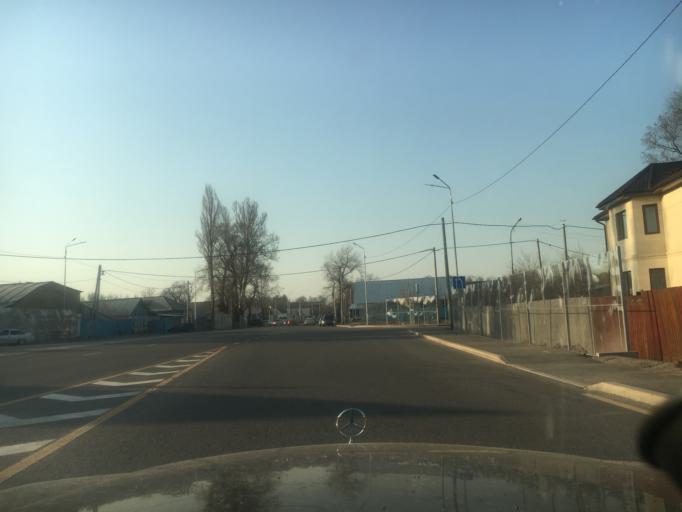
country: KZ
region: Almaty Qalasy
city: Almaty
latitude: 43.2788
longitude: 76.9409
